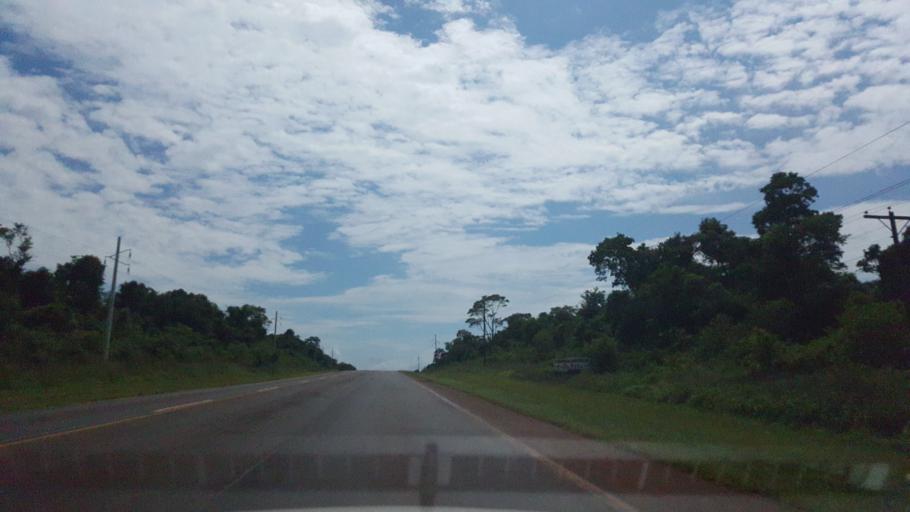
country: AR
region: Misiones
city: Capiovi
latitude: -26.8892
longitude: -55.0549
